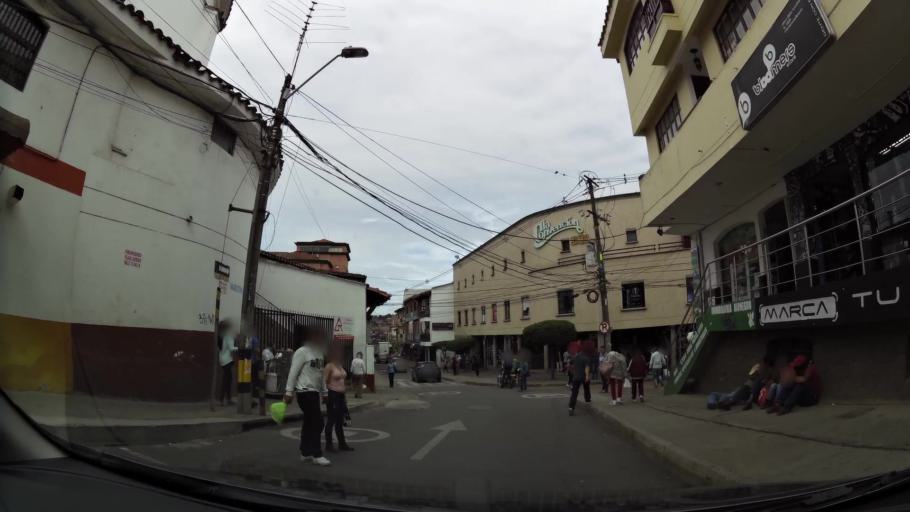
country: CO
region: Antioquia
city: Rionegro
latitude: 6.1531
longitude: -75.3734
